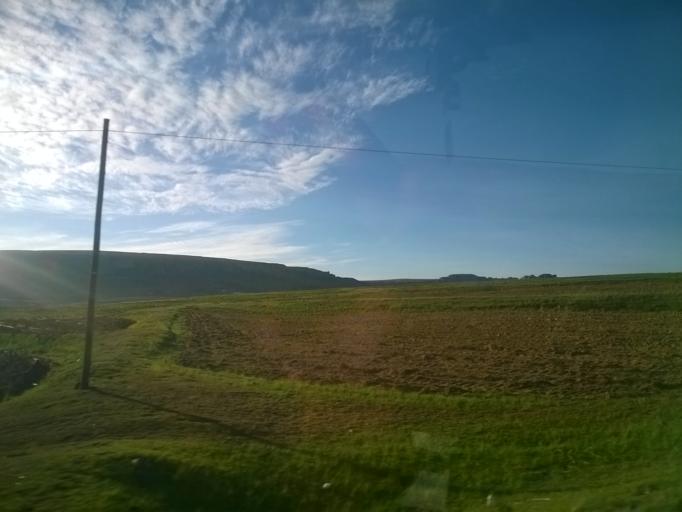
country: LS
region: Berea
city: Teyateyaneng
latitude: -29.1753
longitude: 27.6310
